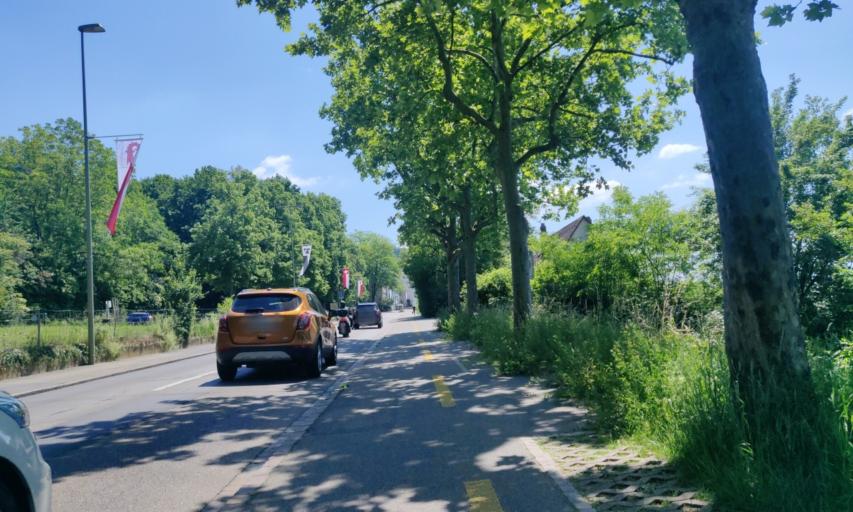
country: CH
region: Basel-Landschaft
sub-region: Bezirk Arlesheim
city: Munchenstein
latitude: 47.5154
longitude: 7.6197
